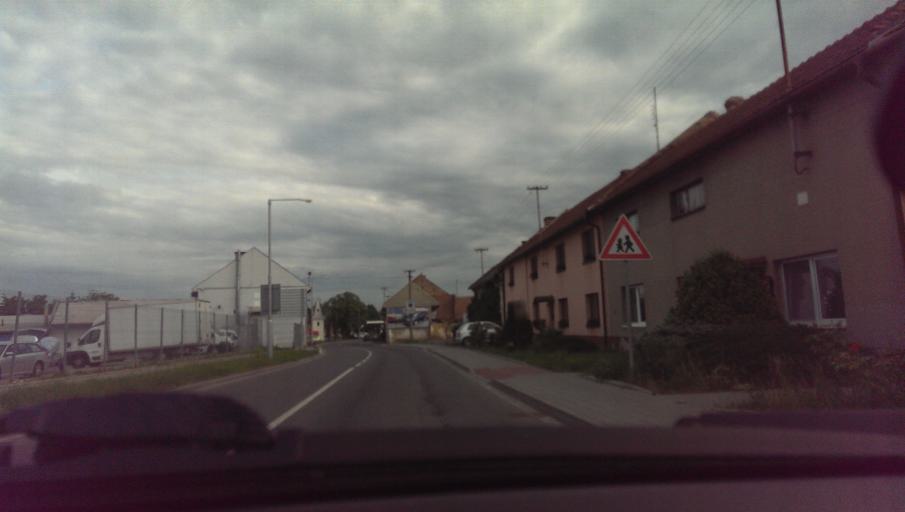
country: CZ
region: Zlin
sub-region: Okres Kromeriz
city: Kromeriz
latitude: 49.2737
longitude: 17.4031
